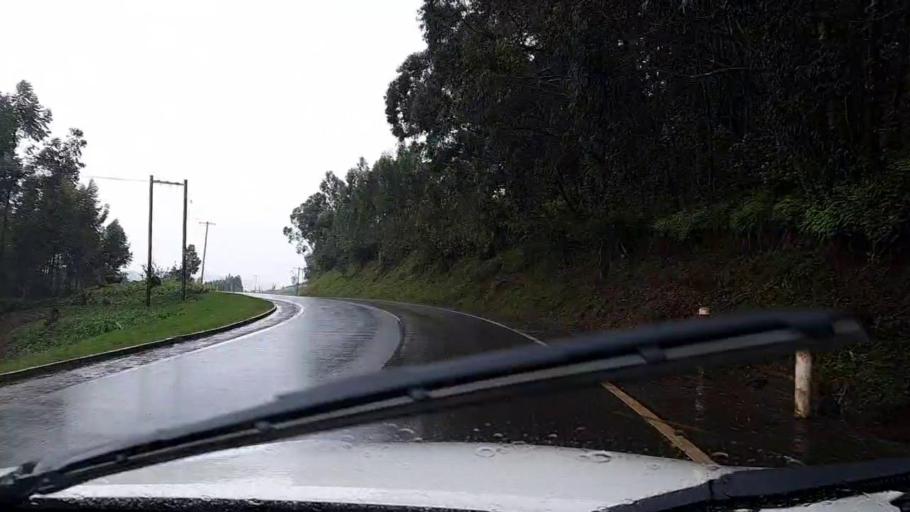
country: RW
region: Western Province
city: Cyangugu
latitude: -2.4623
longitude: 28.9921
